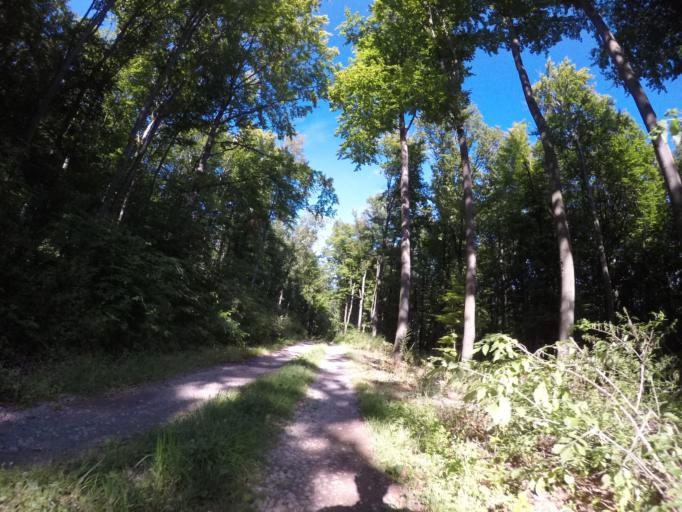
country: SK
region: Kosicky
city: Kosice
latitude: 48.7436
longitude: 21.1892
